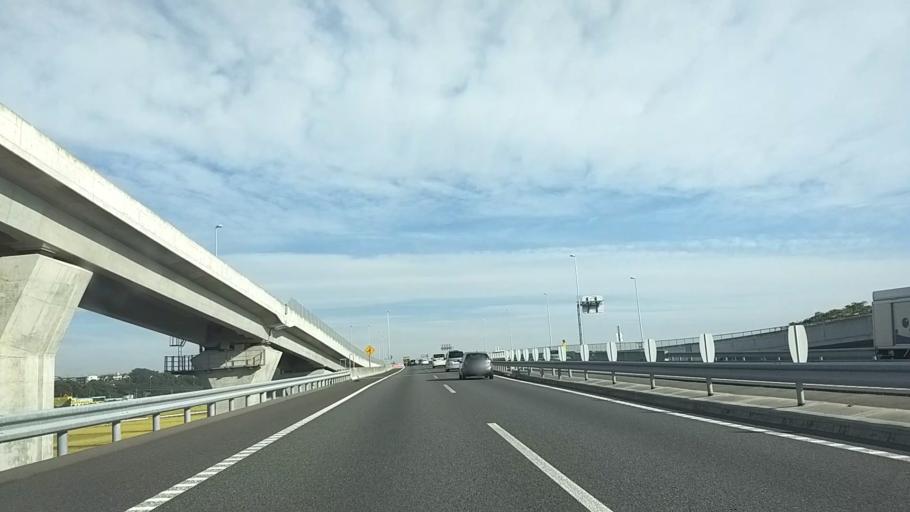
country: JP
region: Kanagawa
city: Zama
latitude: 35.4809
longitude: 139.3724
